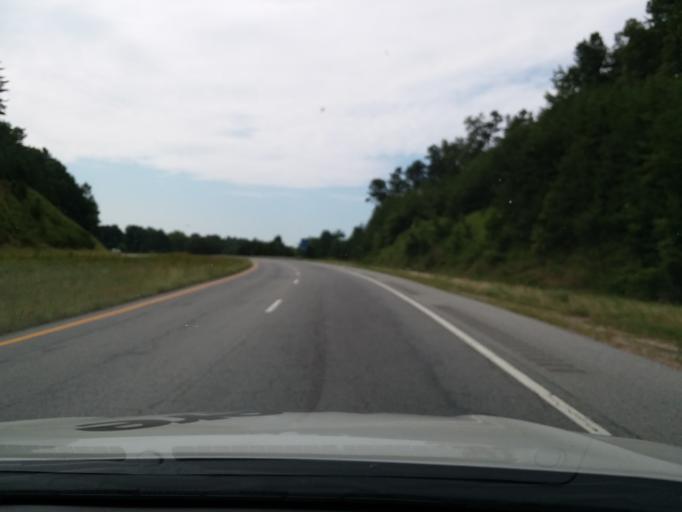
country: US
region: Georgia
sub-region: Rabun County
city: Clayton
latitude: 34.8029
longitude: -83.4263
